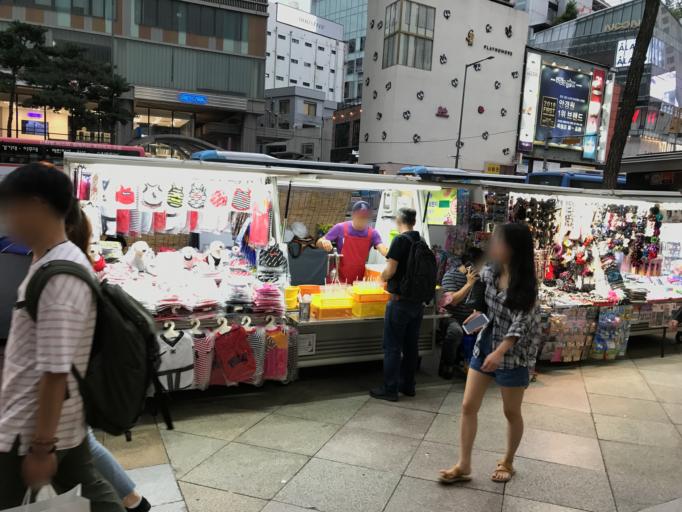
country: KR
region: Seoul
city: Seoul
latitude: 37.5642
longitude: 126.9826
